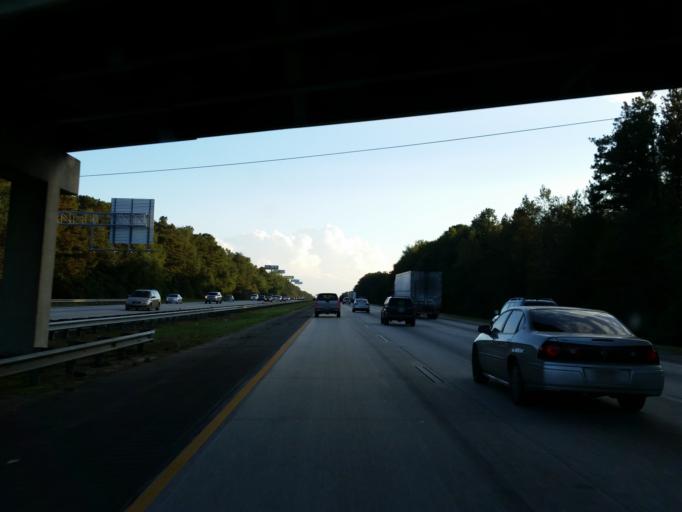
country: US
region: Georgia
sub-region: Peach County
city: Byron
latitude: 32.6431
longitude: -83.7438
